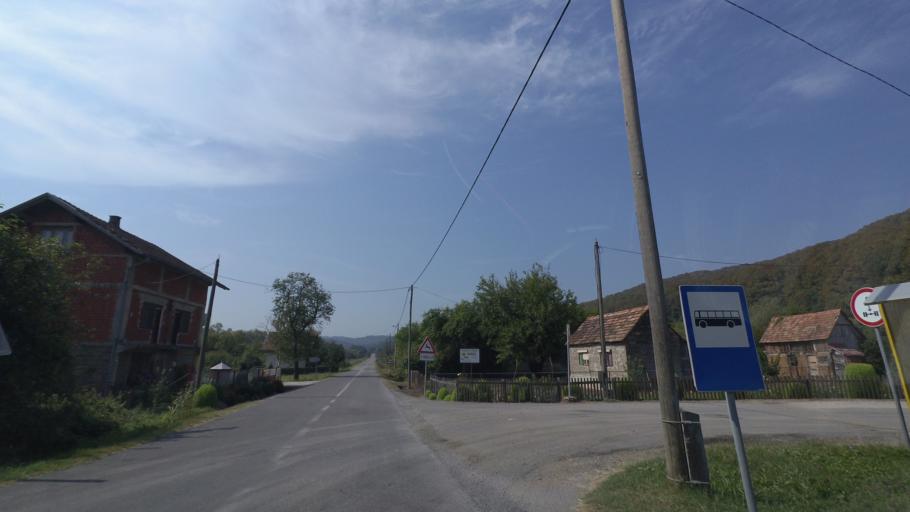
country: BA
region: Republika Srpska
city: Dobrljin
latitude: 45.1909
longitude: 16.4805
